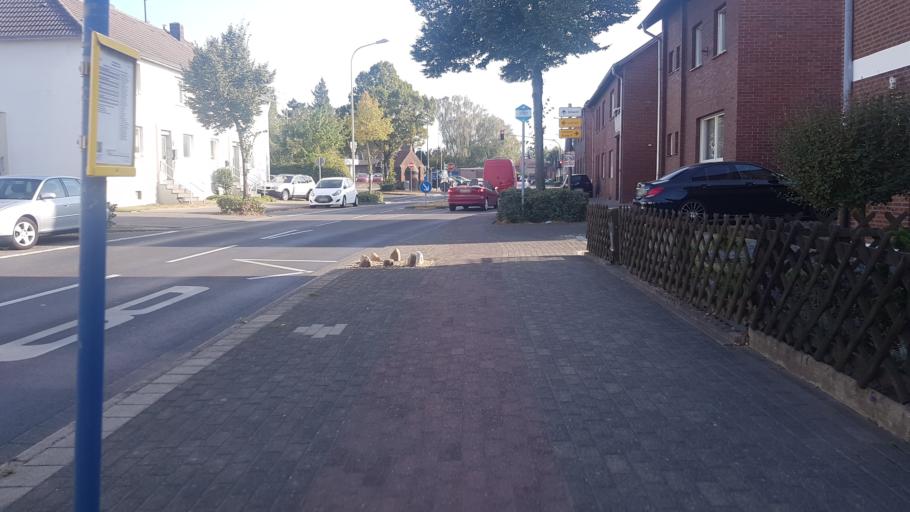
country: DE
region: North Rhine-Westphalia
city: Baesweiler
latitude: 50.8999
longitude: 6.1802
